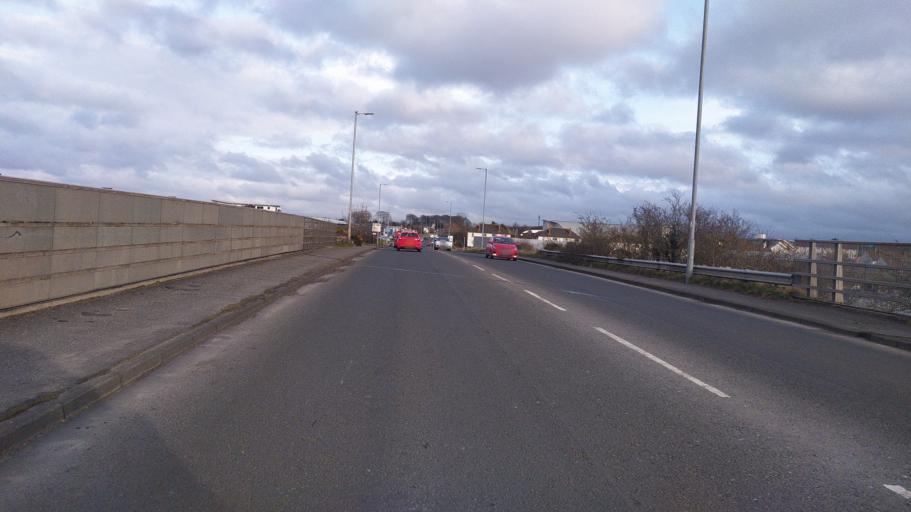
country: GB
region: Scotland
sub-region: South Ayrshire
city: Prestwick
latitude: 55.4774
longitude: -4.5942
